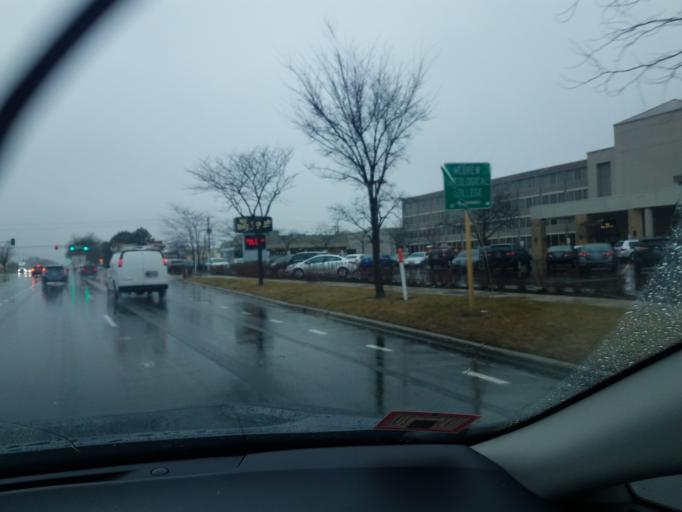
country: US
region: Illinois
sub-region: Cook County
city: Lincolnwood
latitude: 42.0119
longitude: -87.7600
